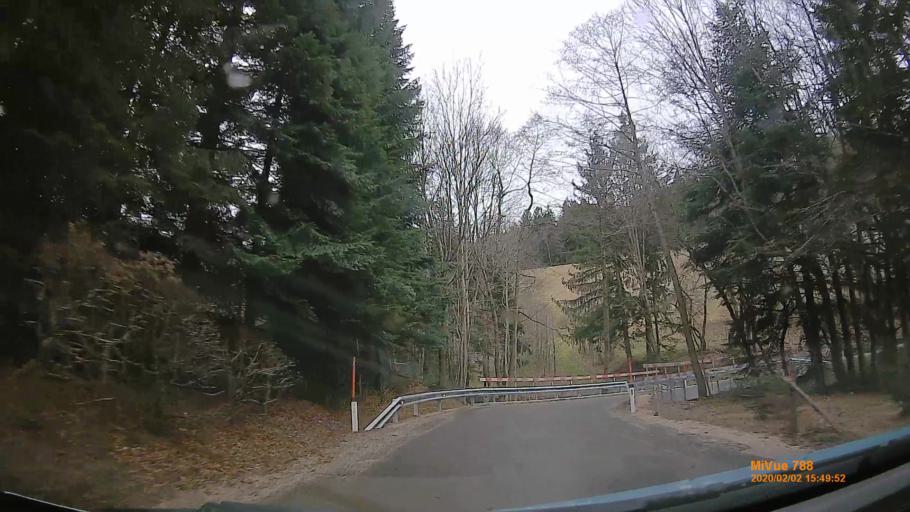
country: AT
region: Lower Austria
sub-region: Politischer Bezirk Neunkirchen
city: Reichenau an der Rax
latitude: 47.6815
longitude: 15.8132
